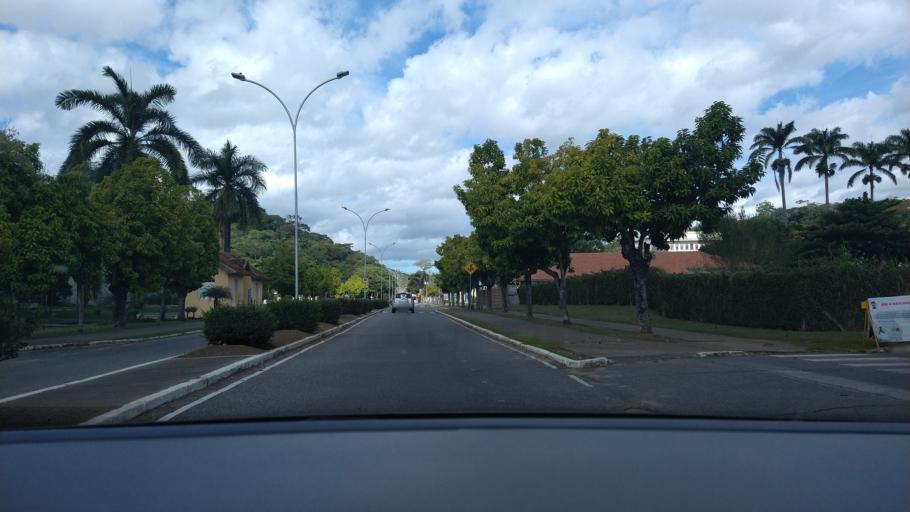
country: BR
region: Minas Gerais
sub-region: Vicosa
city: Vicosa
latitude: -20.7614
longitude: -42.8687
